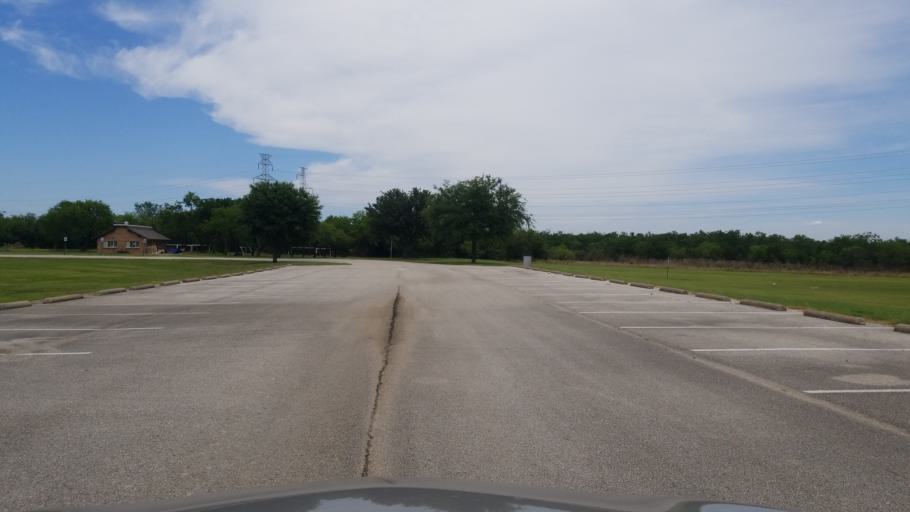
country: US
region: Texas
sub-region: Dallas County
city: Grand Prairie
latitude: 32.6853
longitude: -96.9822
